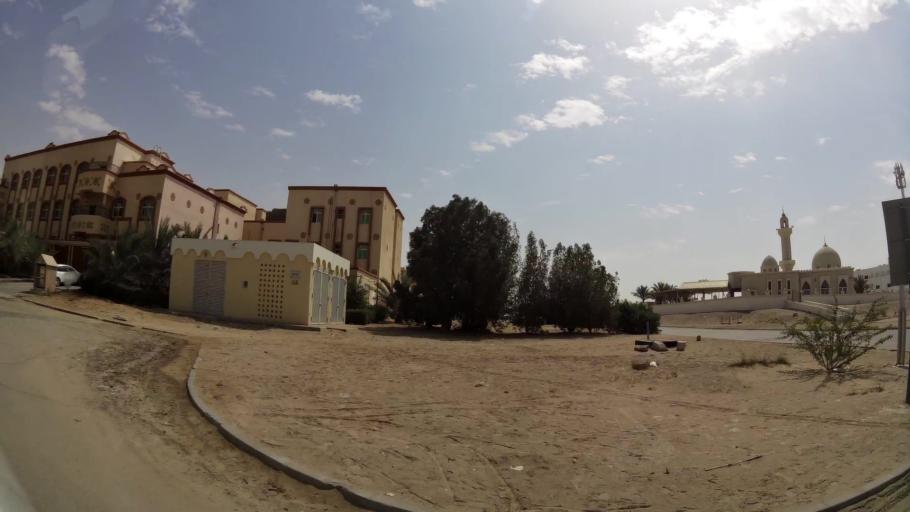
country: AE
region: Abu Dhabi
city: Abu Dhabi
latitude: 24.2986
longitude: 54.6289
